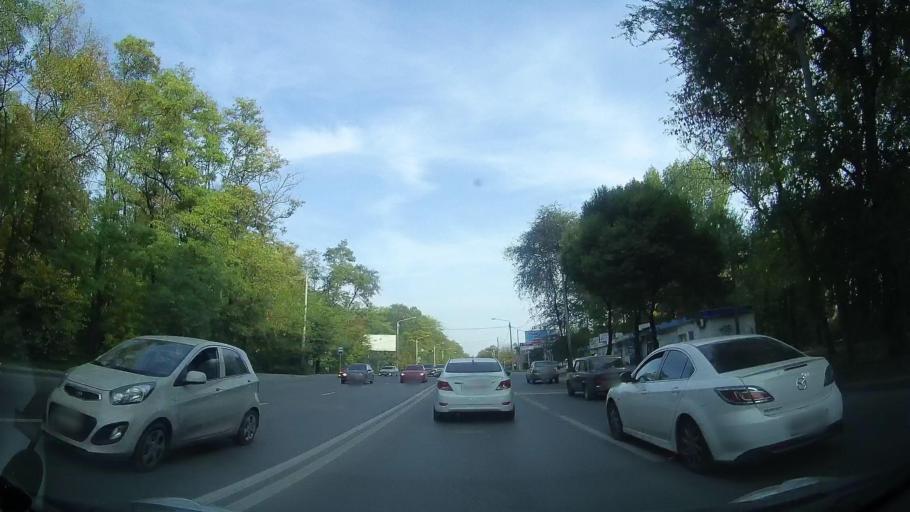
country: RU
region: Rostov
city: Imeni Chkalova
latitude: 47.2774
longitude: 39.7817
